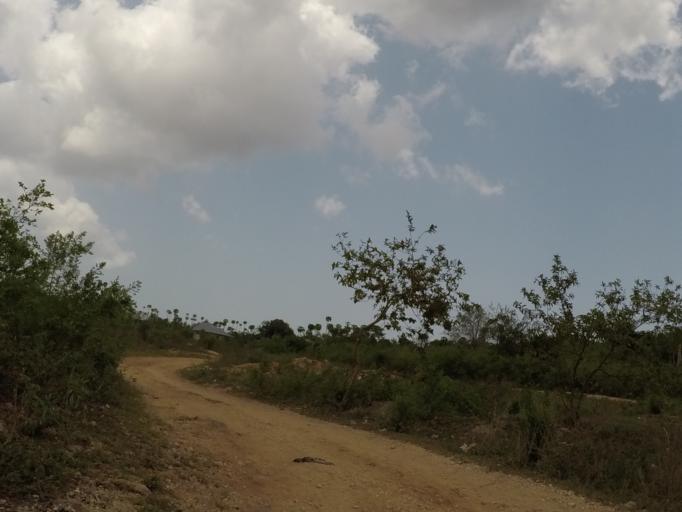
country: TZ
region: Zanzibar Central/South
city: Koani
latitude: -6.1762
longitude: 39.3113
